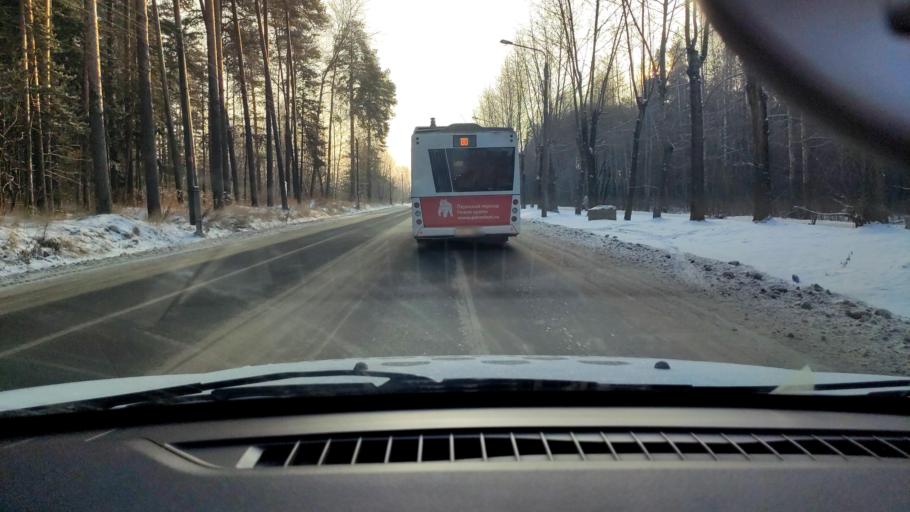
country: RU
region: Perm
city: Kultayevo
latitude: 58.0149
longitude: 55.9820
